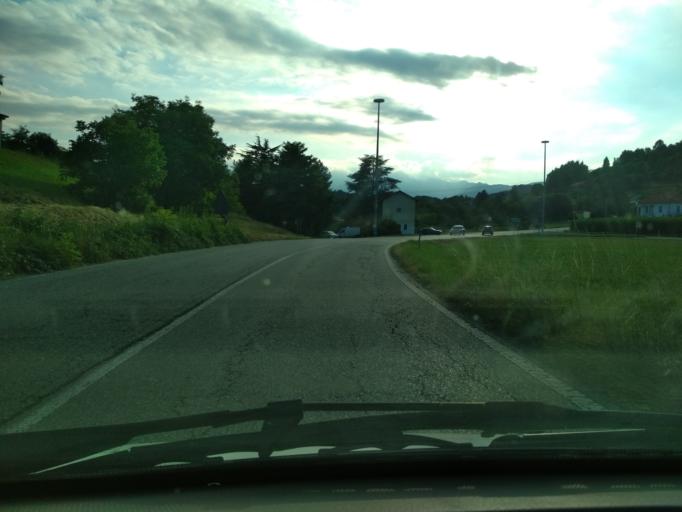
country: IT
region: Piedmont
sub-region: Provincia di Torino
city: Villarbasse
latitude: 45.0397
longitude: 7.4563
